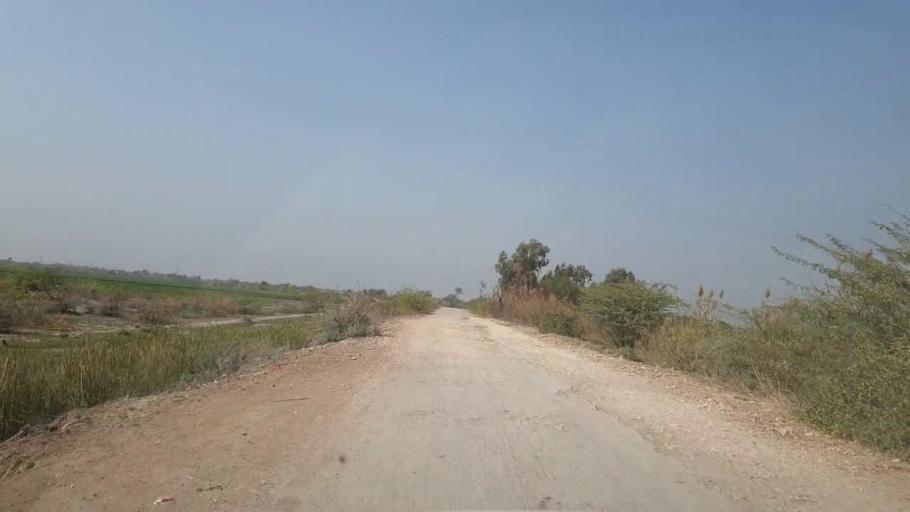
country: PK
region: Sindh
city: Mirpur Khas
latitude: 25.6969
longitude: 69.1464
